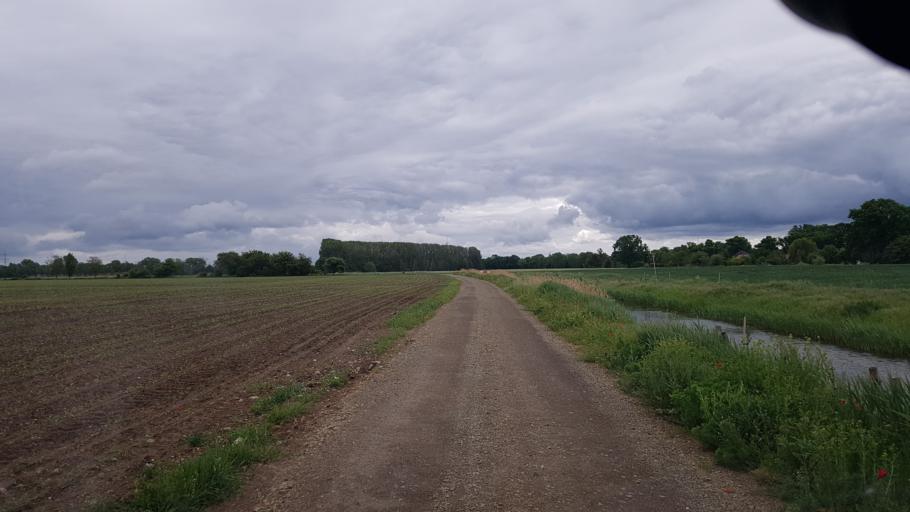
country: DE
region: Brandenburg
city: Doberlug-Kirchhain
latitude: 51.6548
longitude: 13.5485
